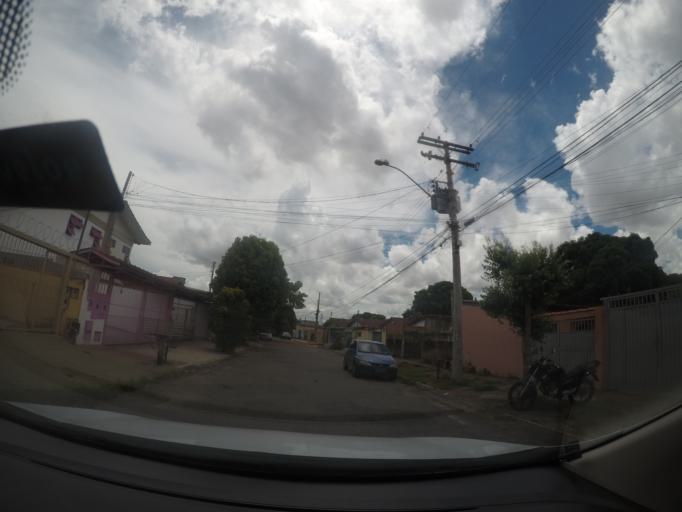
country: BR
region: Goias
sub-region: Goiania
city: Goiania
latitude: -16.6723
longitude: -49.3105
